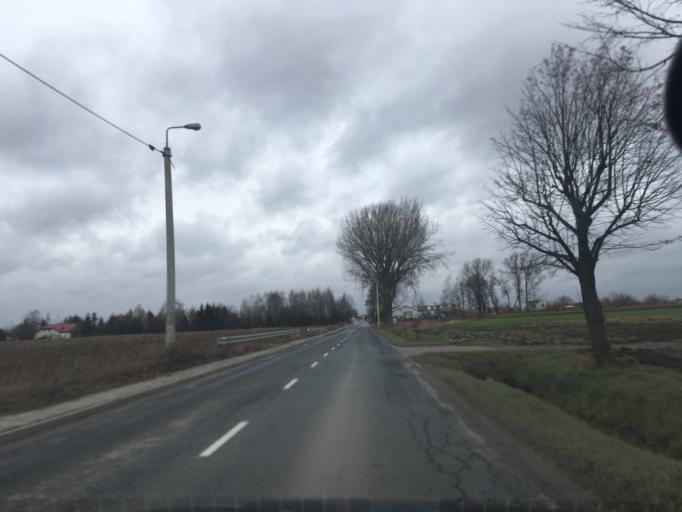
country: PL
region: Masovian Voivodeship
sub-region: Powiat piaseczynski
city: Lesznowola
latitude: 52.0979
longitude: 20.9331
